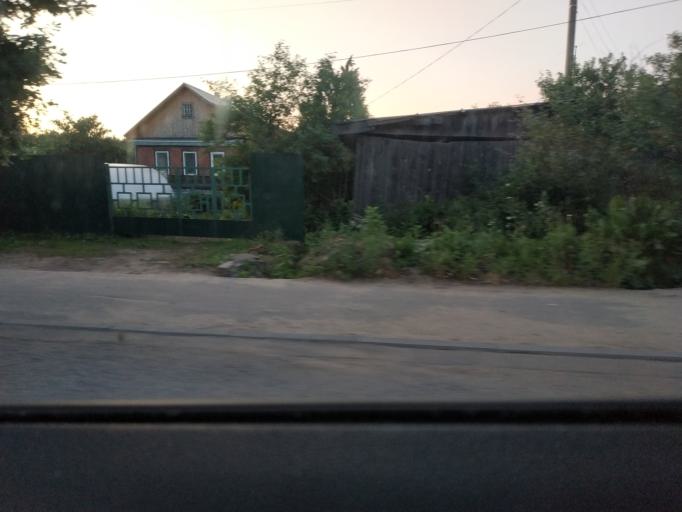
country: RU
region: Moskovskaya
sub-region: Shchelkovskiy Rayon
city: Grebnevo
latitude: 55.9737
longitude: 38.0994
